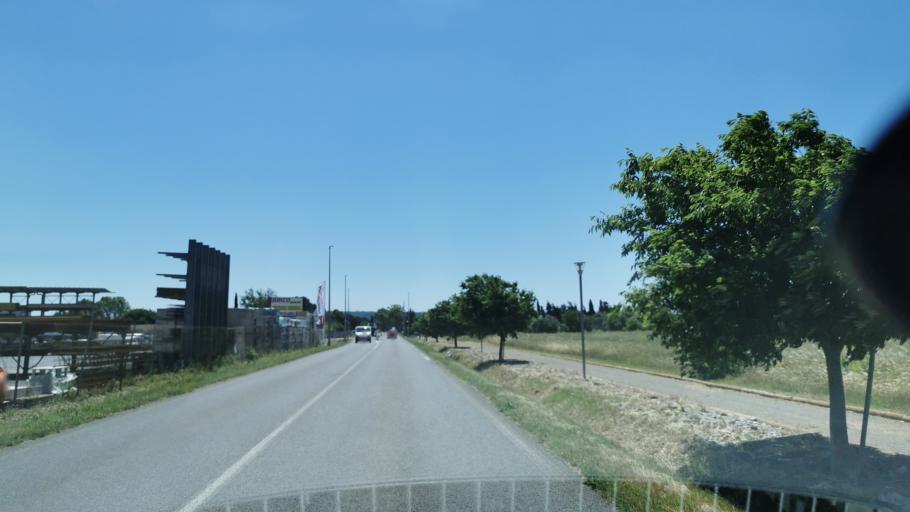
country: FR
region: Languedoc-Roussillon
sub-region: Departement de l'Aude
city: Saint-Marcel-sur-Aude
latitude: 43.2548
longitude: 2.9117
